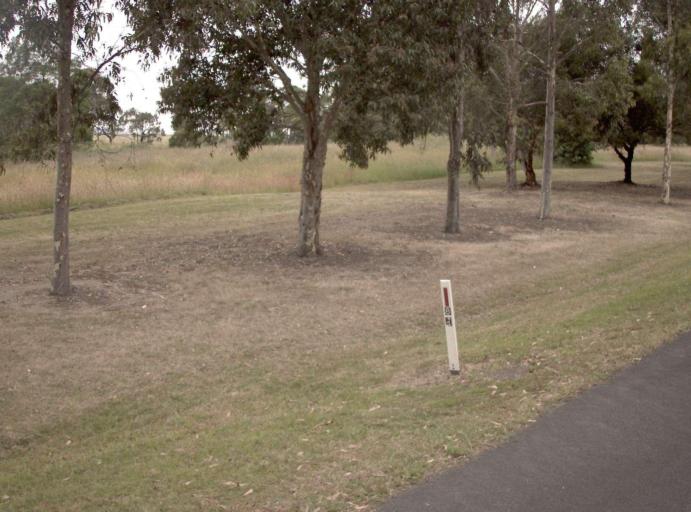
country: AU
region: Victoria
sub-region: Latrobe
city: Morwell
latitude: -38.3031
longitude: 146.4196
